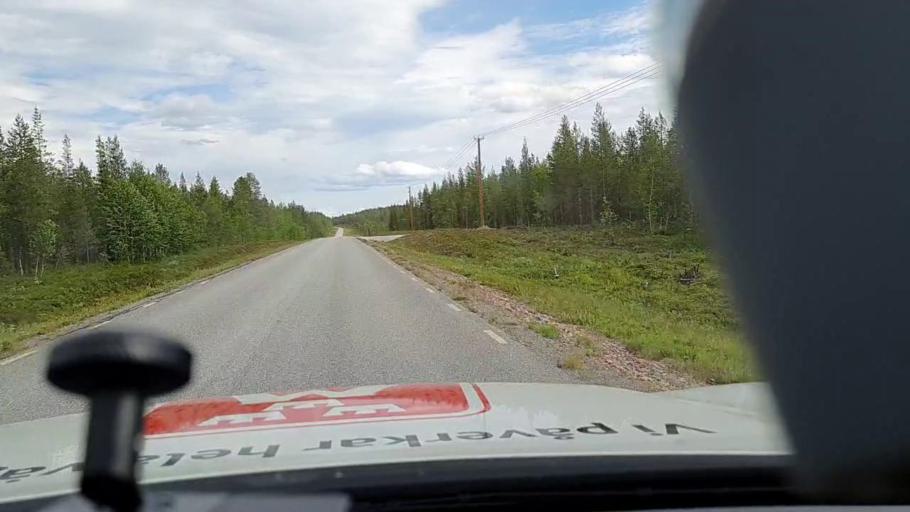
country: SE
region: Norrbotten
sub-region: Jokkmokks Kommun
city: Jokkmokk
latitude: 66.6565
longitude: 19.9756
